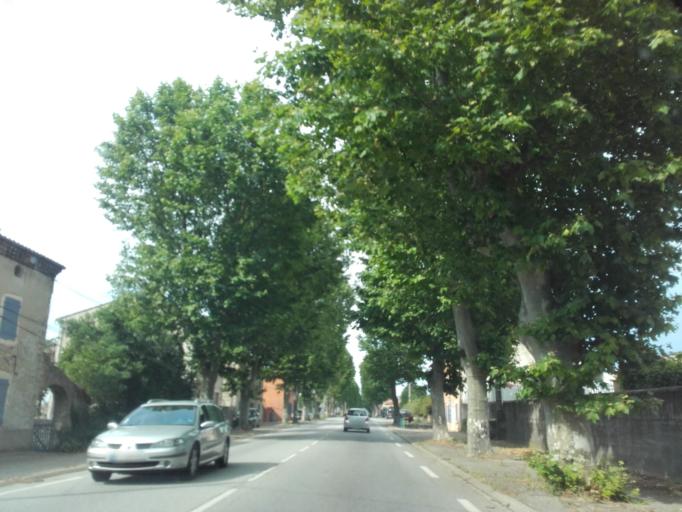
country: FR
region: Rhone-Alpes
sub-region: Departement de l'Ardeche
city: Cruas
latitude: 44.6401
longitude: 4.7758
